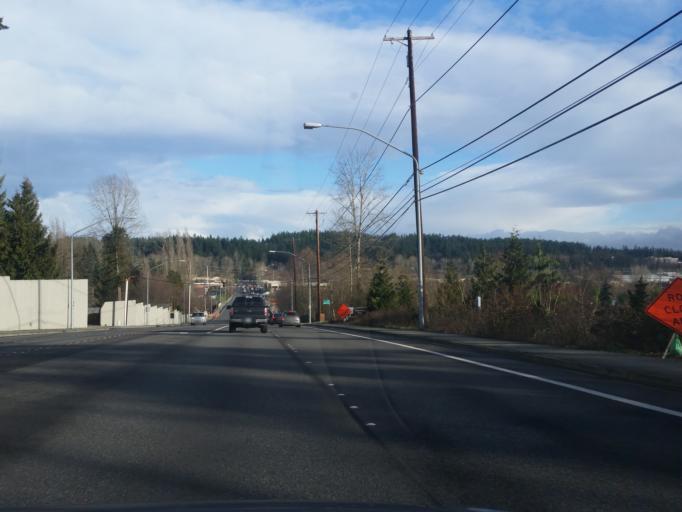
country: US
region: Washington
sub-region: Snohomish County
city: North Creek
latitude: 47.8094
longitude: -122.2178
